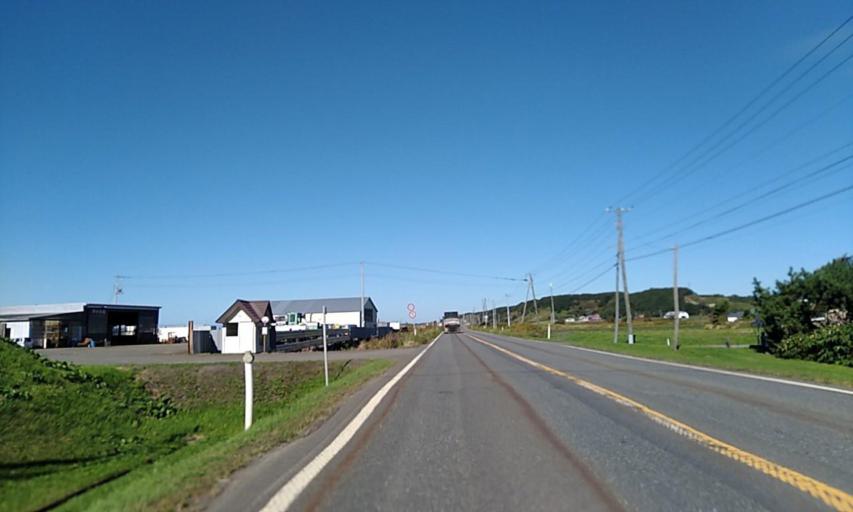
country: JP
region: Hokkaido
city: Shizunai-furukawacho
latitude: 42.4590
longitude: 142.1724
